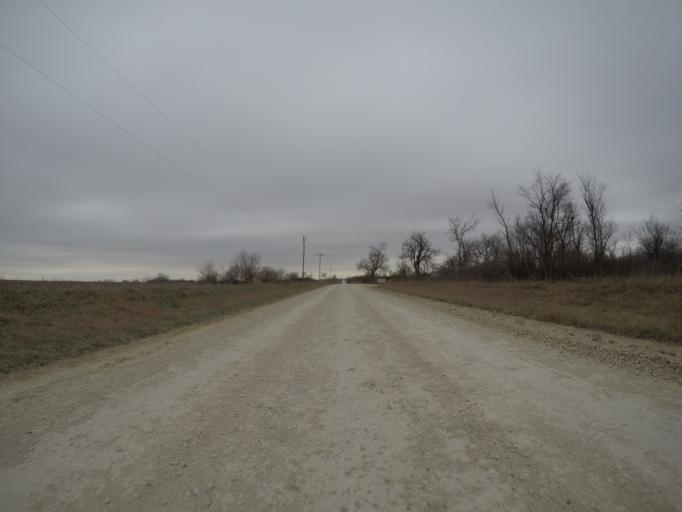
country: US
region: Kansas
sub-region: Wabaunsee County
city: Alma
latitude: 38.8416
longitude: -96.1133
